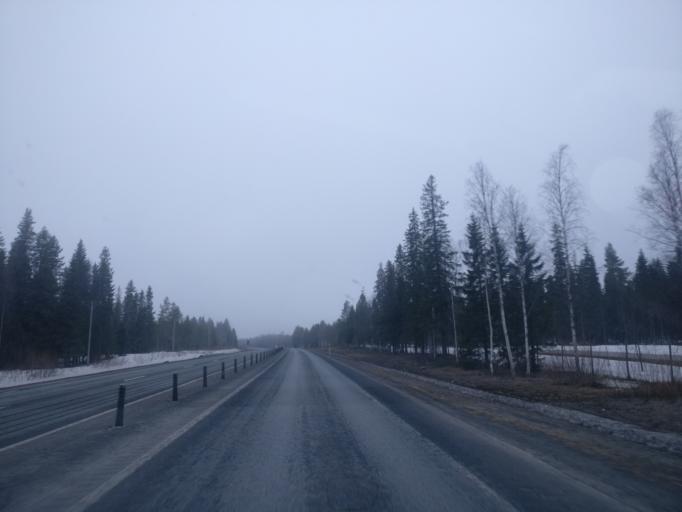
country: FI
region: Lapland
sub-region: Kemi-Tornio
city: Simo
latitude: 65.6670
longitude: 24.9773
